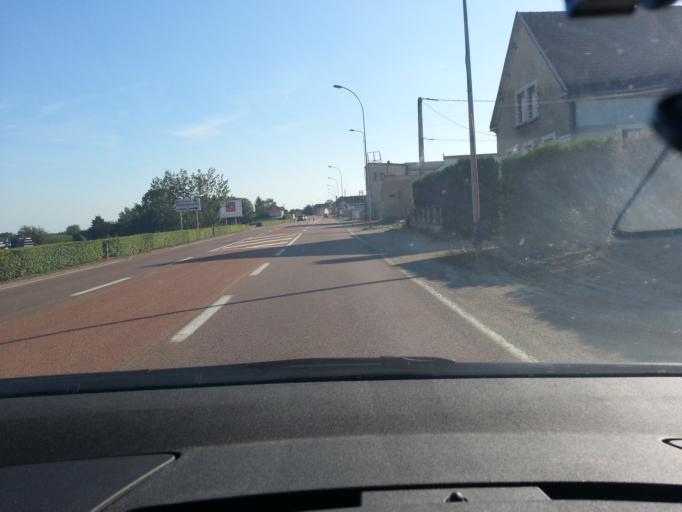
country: FR
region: Bourgogne
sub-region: Departement de la Cote-d'Or
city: Nuits-Saint-Georges
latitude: 47.1012
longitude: 4.9164
